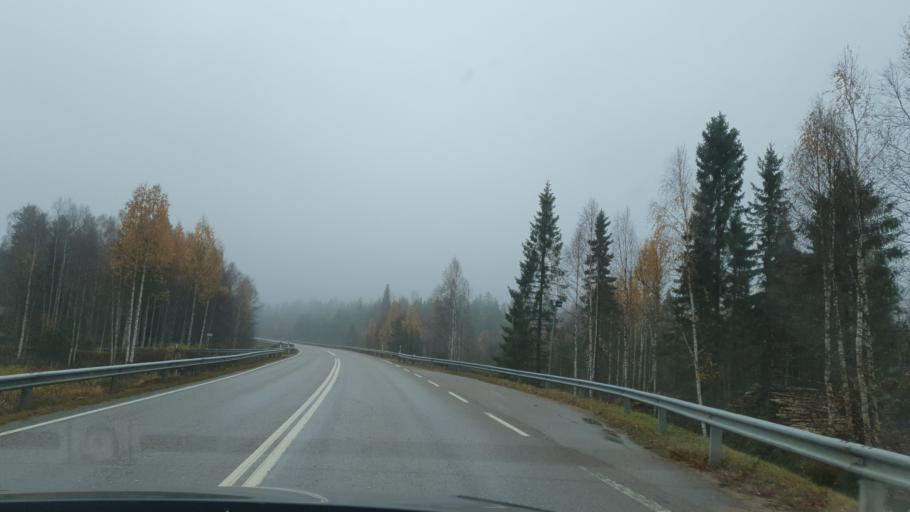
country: FI
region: Lapland
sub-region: Rovaniemi
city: Rovaniemi
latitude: 66.8162
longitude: 25.3960
